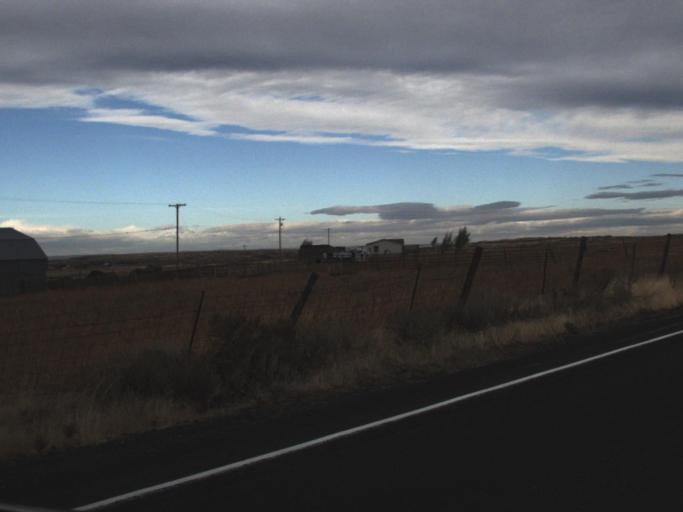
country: US
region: Washington
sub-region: Okanogan County
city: Coulee Dam
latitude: 47.6752
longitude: -118.7217
